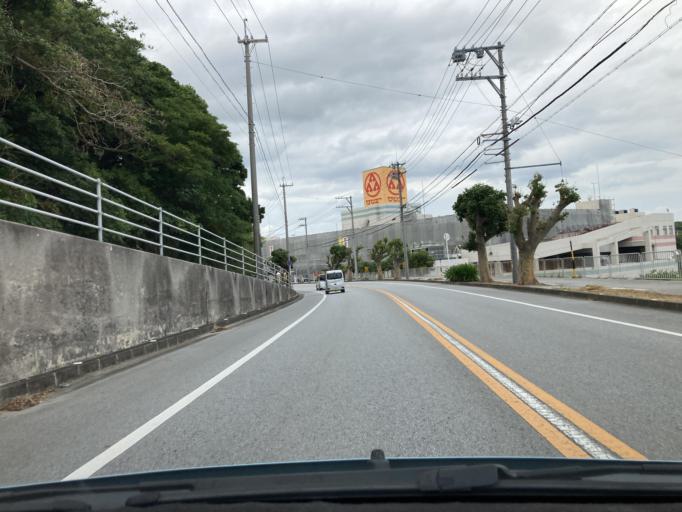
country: JP
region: Okinawa
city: Tomigusuku
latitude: 26.1738
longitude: 127.6893
